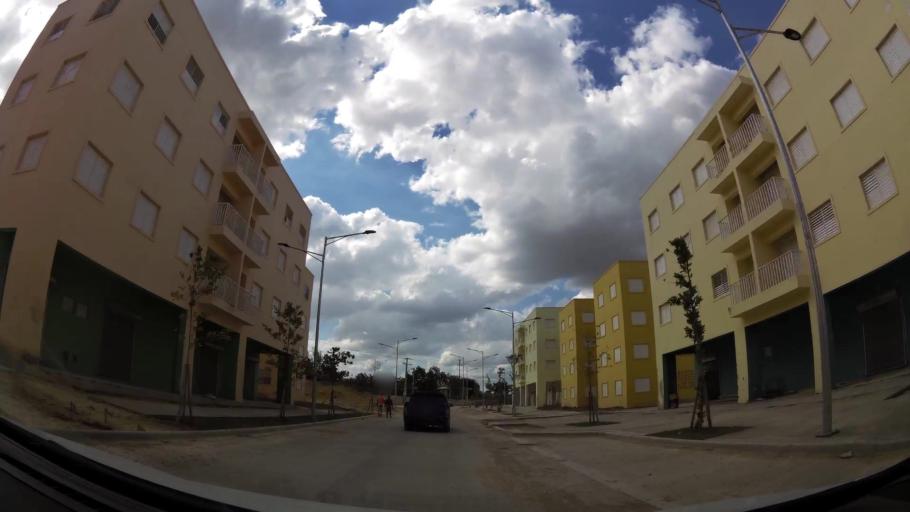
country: DO
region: Nacional
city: Ensanche Luperon
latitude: 18.5287
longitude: -69.8844
